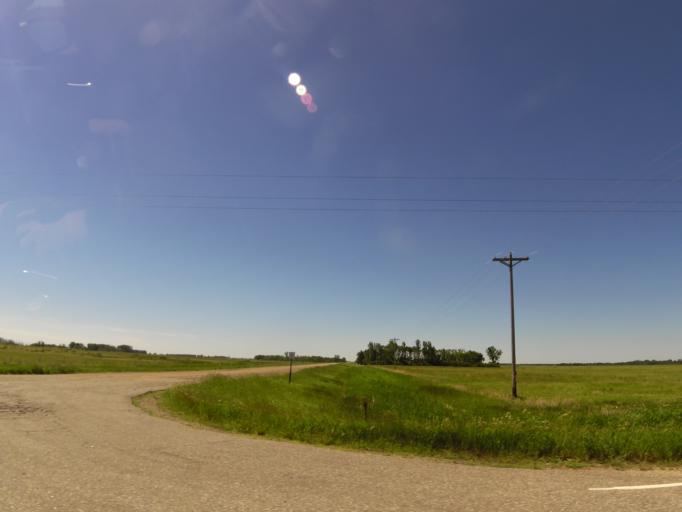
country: US
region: Minnesota
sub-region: Red Lake County
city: Red Lake Falls
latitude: 47.7604
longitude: -96.3953
